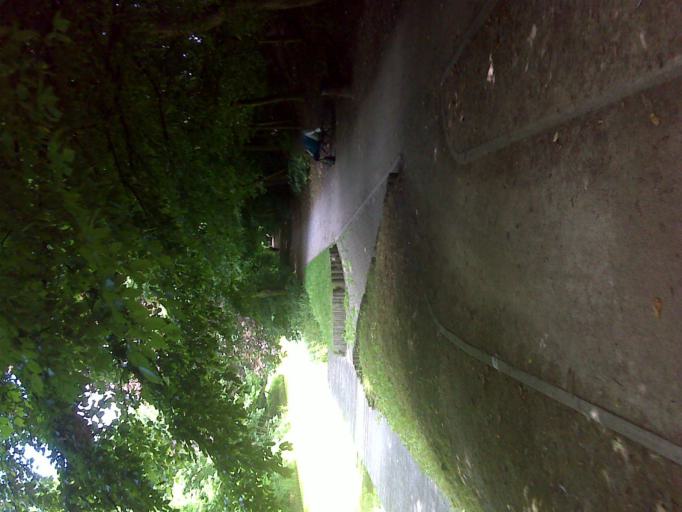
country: FR
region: Nord-Pas-de-Calais
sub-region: Departement du Nord
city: Roubaix
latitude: 50.7032
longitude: 3.1567
